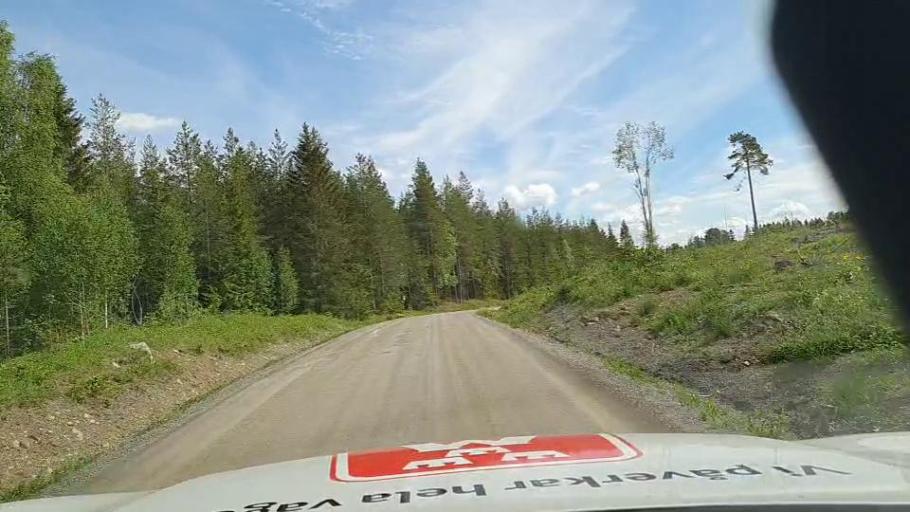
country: SE
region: Jaemtland
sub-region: OEstersunds Kommun
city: Brunflo
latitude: 63.0125
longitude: 14.7805
